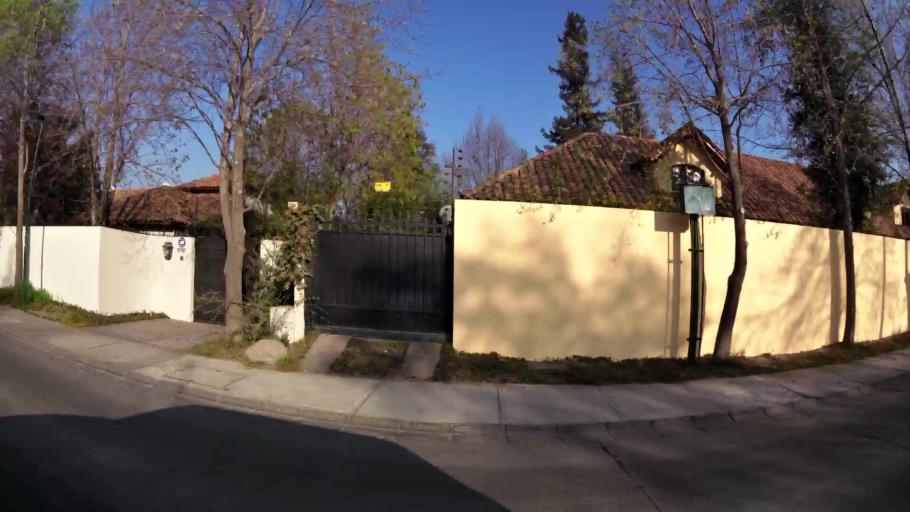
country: CL
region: Santiago Metropolitan
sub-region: Provincia de Santiago
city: Villa Presidente Frei, Nunoa, Santiago, Chile
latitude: -33.3533
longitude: -70.5363
